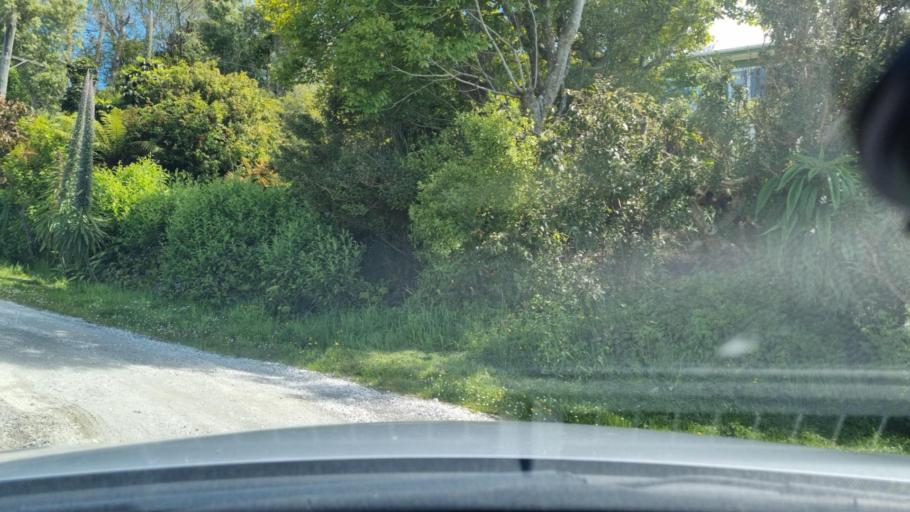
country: NZ
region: Southland
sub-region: Invercargill City
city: Bluff
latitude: -46.5759
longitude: 168.2983
